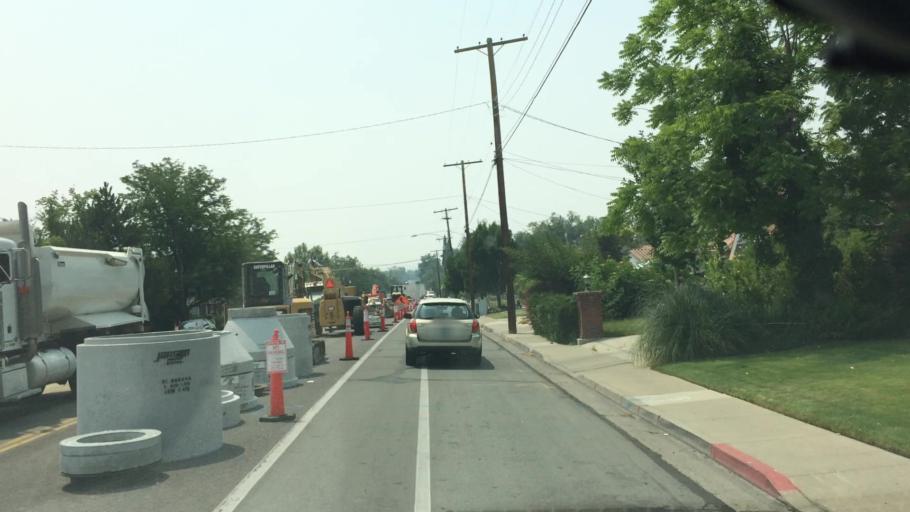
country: US
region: Nevada
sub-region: Washoe County
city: Reno
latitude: 39.5122
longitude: -119.8173
